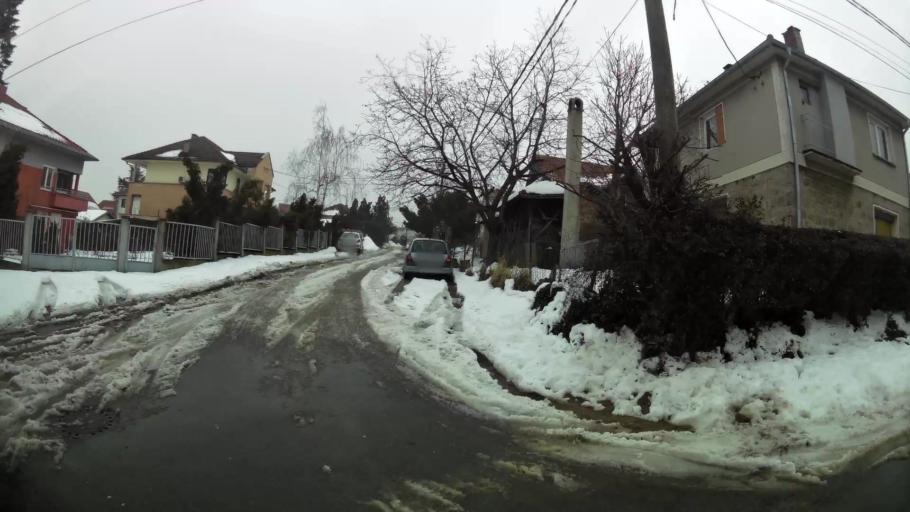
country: RS
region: Central Serbia
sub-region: Belgrade
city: Zvezdara
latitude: 44.7409
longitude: 20.5021
